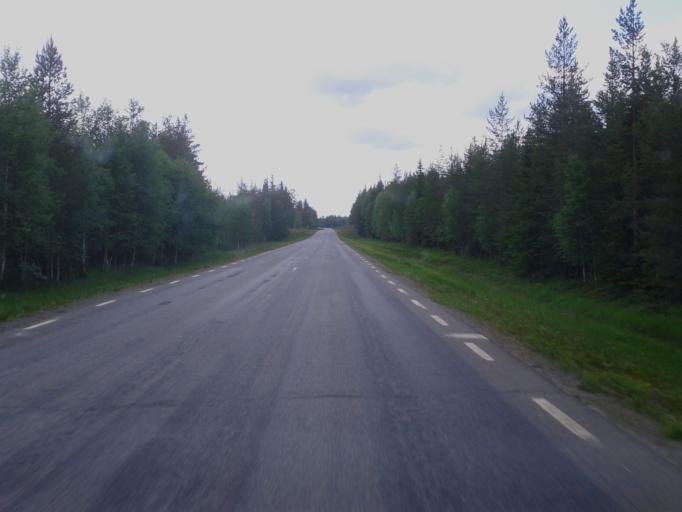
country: SE
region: Vaesterbotten
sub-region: Mala Kommun
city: Mala
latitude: 65.2182
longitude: 18.6573
